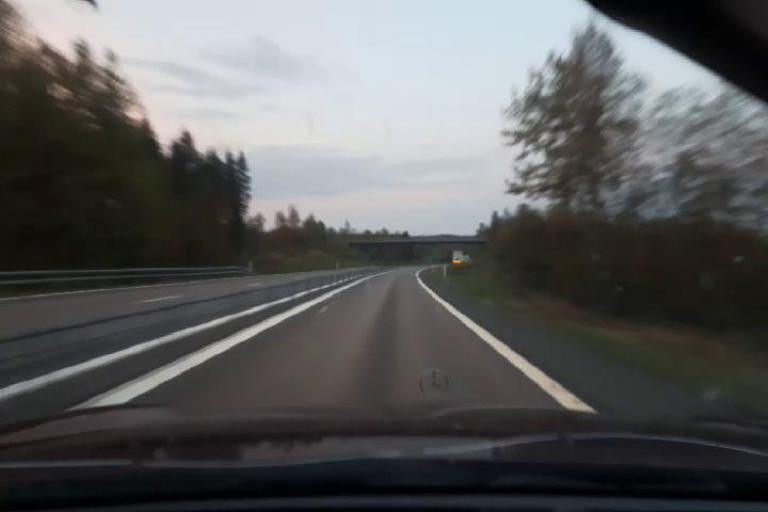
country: SE
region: Vaesternorrland
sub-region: Haernoesands Kommun
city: Haernoesand
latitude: 62.8741
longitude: 18.0513
